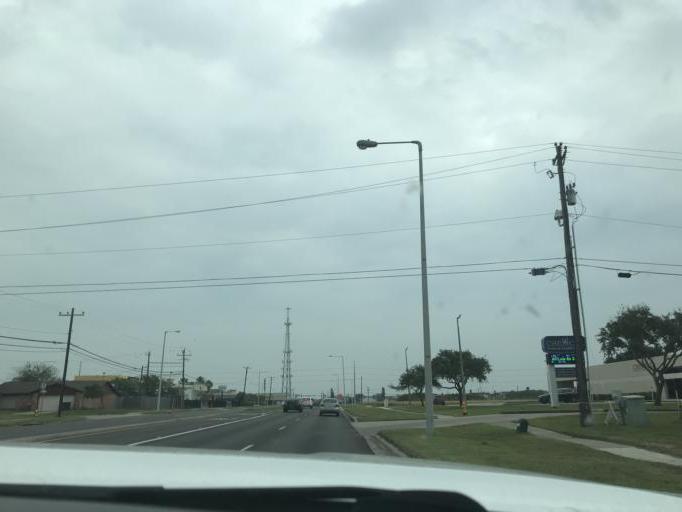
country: US
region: Texas
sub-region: Nueces County
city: Corpus Christi
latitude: 27.6731
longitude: -97.3590
